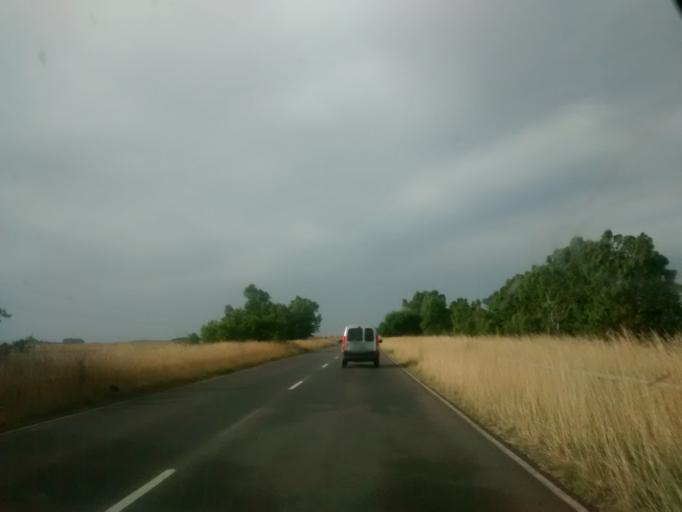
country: AR
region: Buenos Aires
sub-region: Partido de Ayacucho
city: Ayacucho
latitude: -36.7065
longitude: -58.5745
